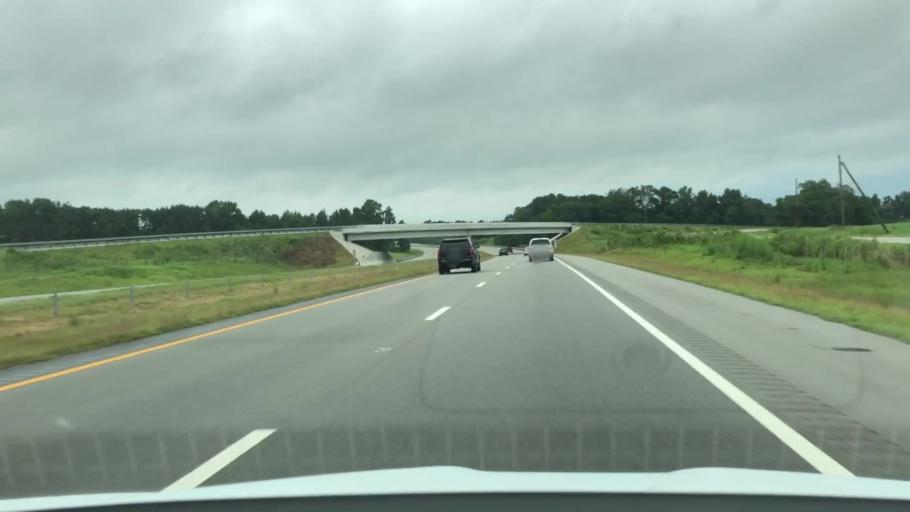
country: US
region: North Carolina
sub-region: Wayne County
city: Elroy
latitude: 35.3539
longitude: -77.8483
